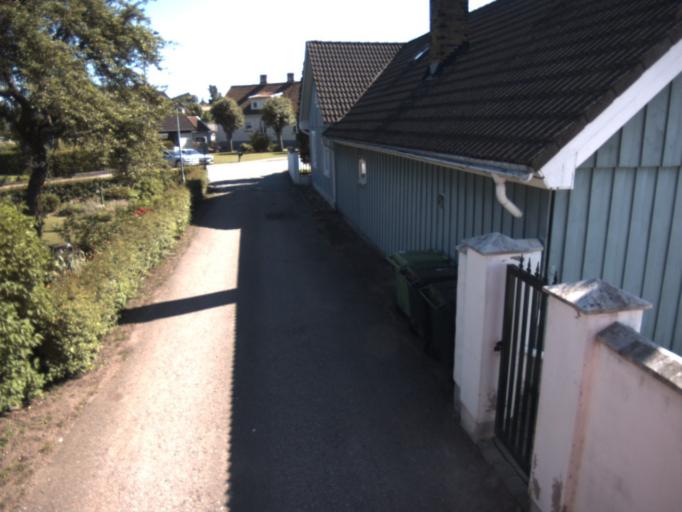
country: SE
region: Skane
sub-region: Helsingborg
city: Gantofta
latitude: 55.9922
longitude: 12.8043
